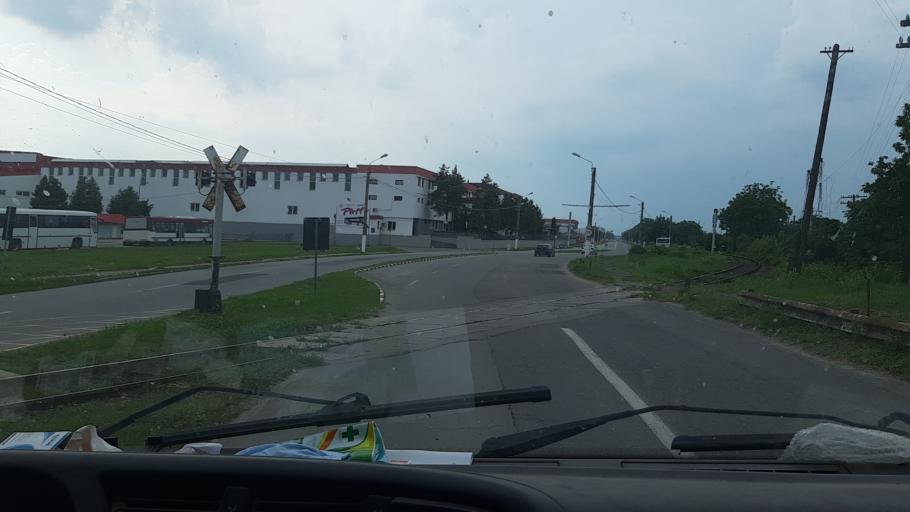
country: RO
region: Timis
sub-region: Municipiul Lugoj
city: Lugoj
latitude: 45.7011
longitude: 21.8936
